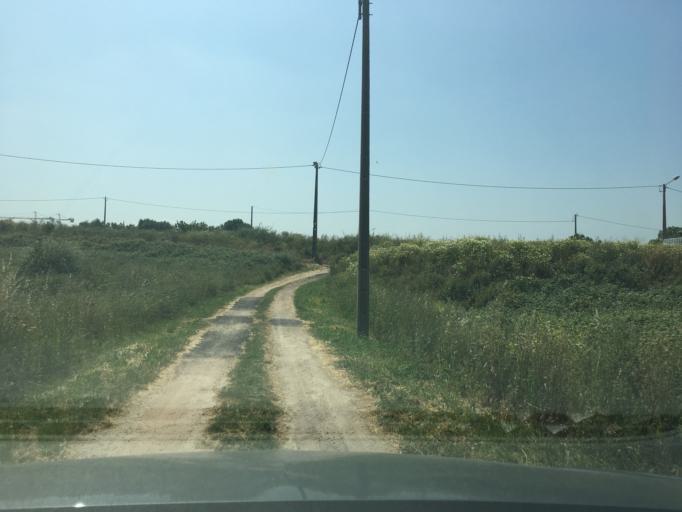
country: PT
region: Lisbon
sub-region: Oeiras
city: Porto Salvo
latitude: 38.7076
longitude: -9.3097
